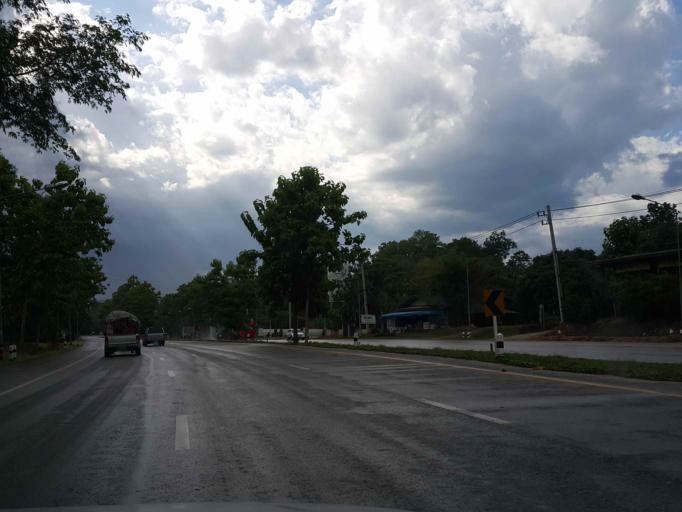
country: TH
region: Lampang
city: Thoen
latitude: 17.6588
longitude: 99.2495
